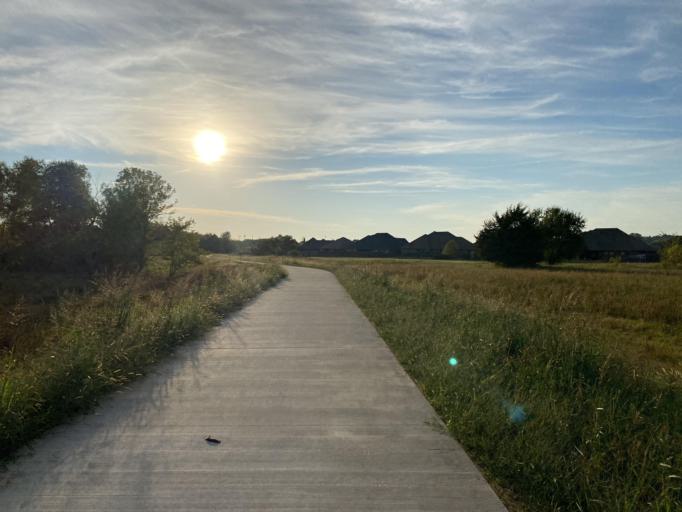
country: US
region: Arkansas
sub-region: Washington County
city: Johnson
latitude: 36.1046
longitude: -94.1984
